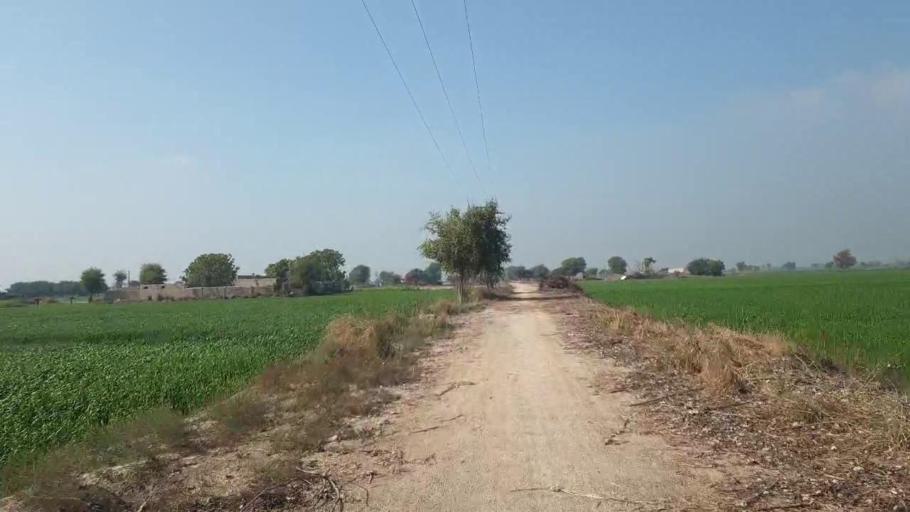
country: PK
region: Sindh
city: Shahdadpur
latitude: 26.0208
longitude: 68.5722
